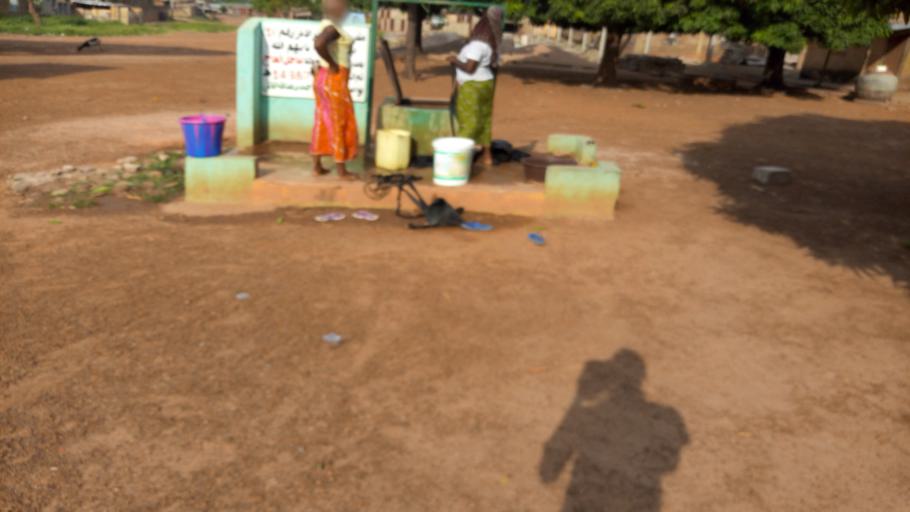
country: CI
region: Vallee du Bandama
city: Bouake
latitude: 7.7094
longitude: -5.0017
